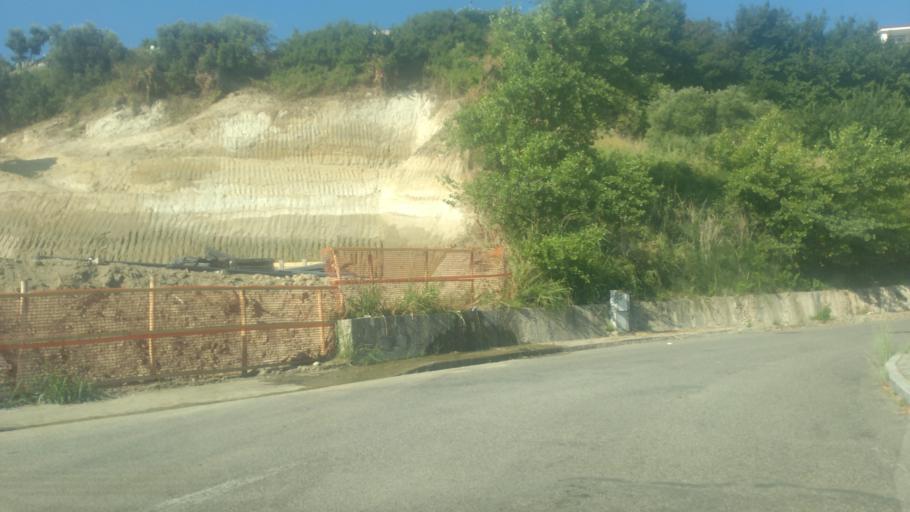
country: IT
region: Calabria
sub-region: Provincia di Catanzaro
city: Soverato Superiore
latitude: 38.7003
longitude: 16.5375
